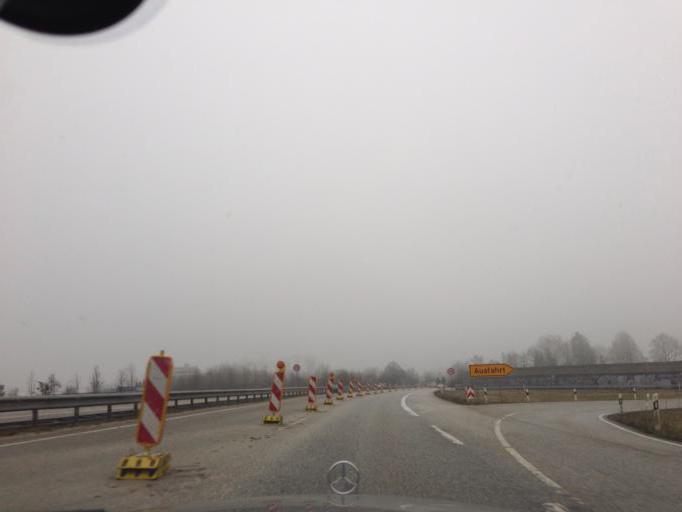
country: DE
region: Schleswig-Holstein
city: Klein Barkau
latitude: 54.2765
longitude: 10.1423
